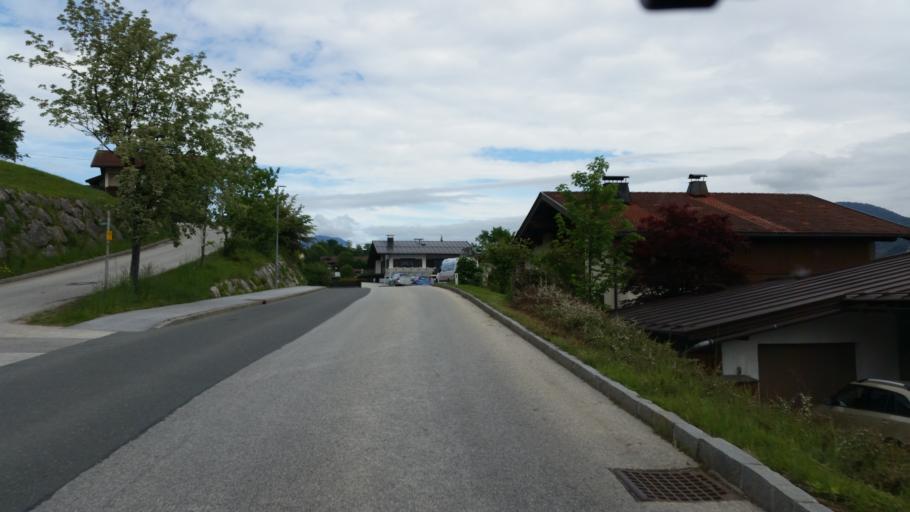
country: AT
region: Tyrol
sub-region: Politischer Bezirk Kufstein
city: Breitenbach am Inn
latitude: 47.4841
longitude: 11.9860
